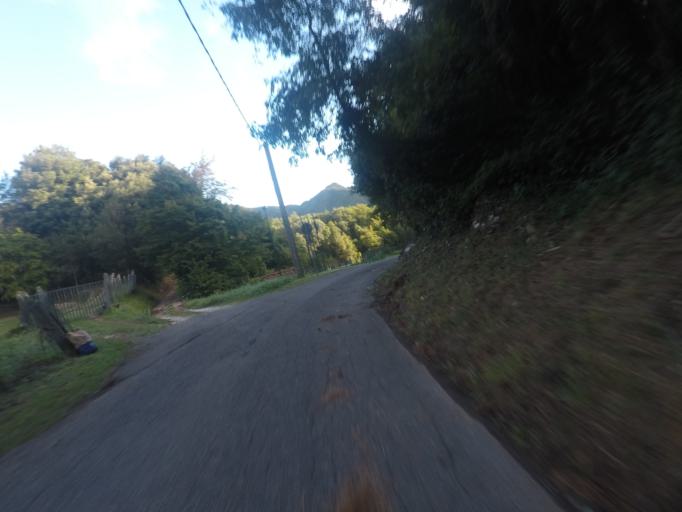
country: IT
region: Tuscany
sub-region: Provincia di Lucca
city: Pescaglia
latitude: 43.9377
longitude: 10.3827
